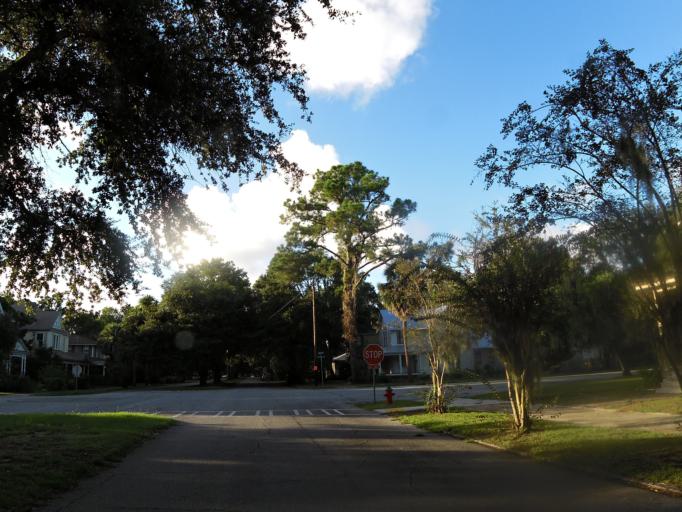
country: US
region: Georgia
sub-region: Glynn County
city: Brunswick
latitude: 31.1385
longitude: -81.4893
